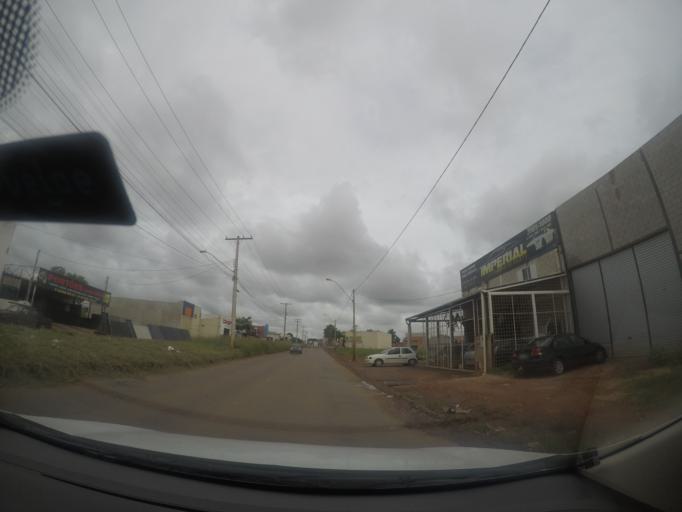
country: BR
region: Goias
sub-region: Goiania
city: Goiania
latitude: -16.6855
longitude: -49.3712
